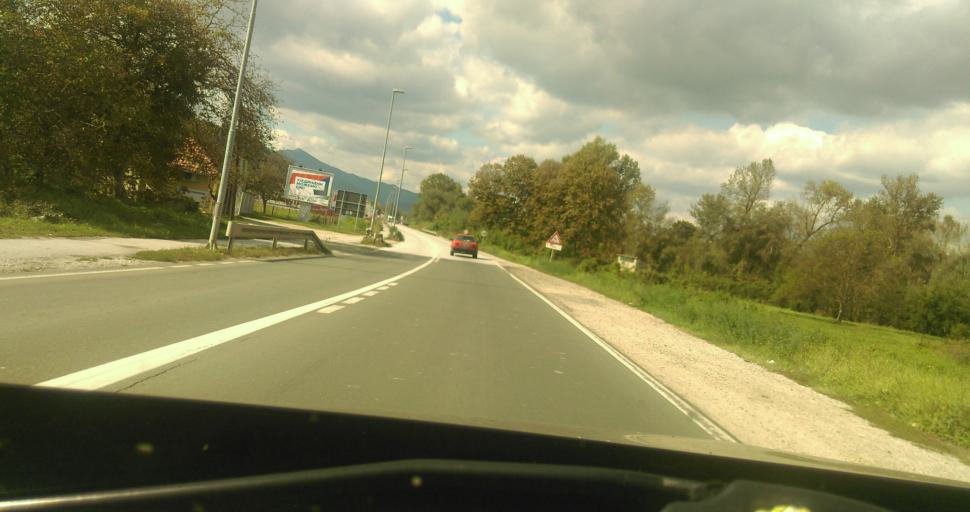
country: RS
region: Central Serbia
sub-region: Moravicki Okrug
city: Cacak
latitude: 43.8909
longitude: 20.3120
